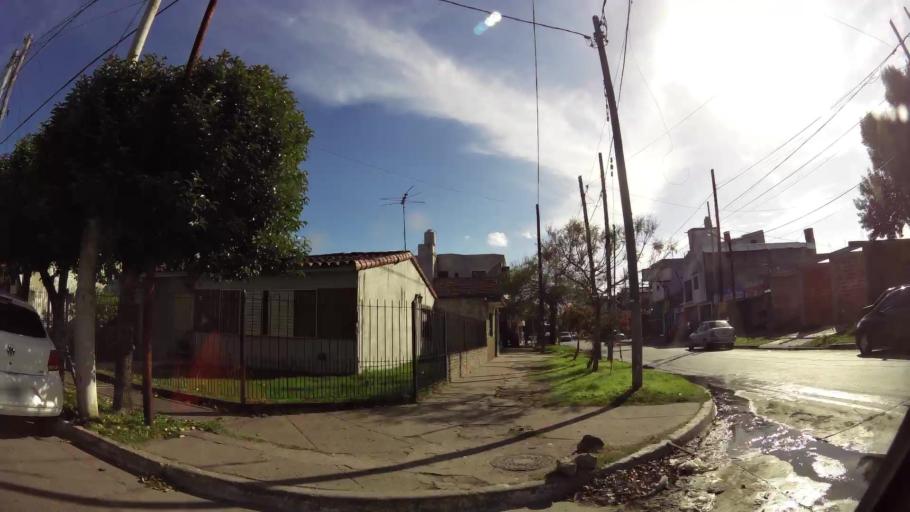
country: AR
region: Buenos Aires
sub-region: Partido de Quilmes
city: Quilmes
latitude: -34.7931
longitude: -58.2329
